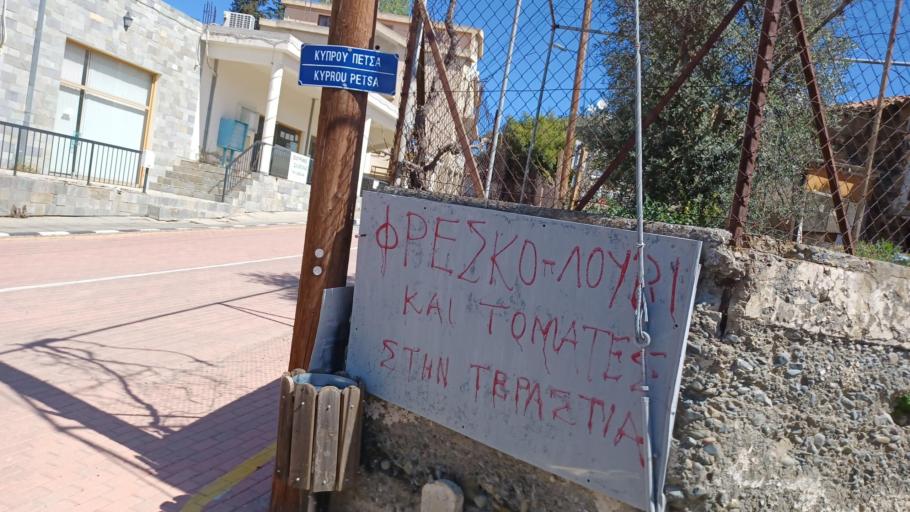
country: CY
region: Lefkosia
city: Peristerona
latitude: 35.0494
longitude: 33.0569
